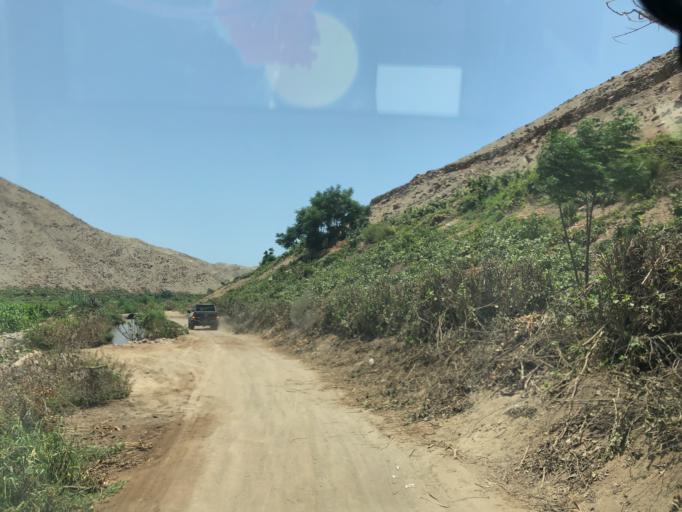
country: PE
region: Lima
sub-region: Provincia de Canete
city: Quilmana
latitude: -12.9892
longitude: -76.4359
